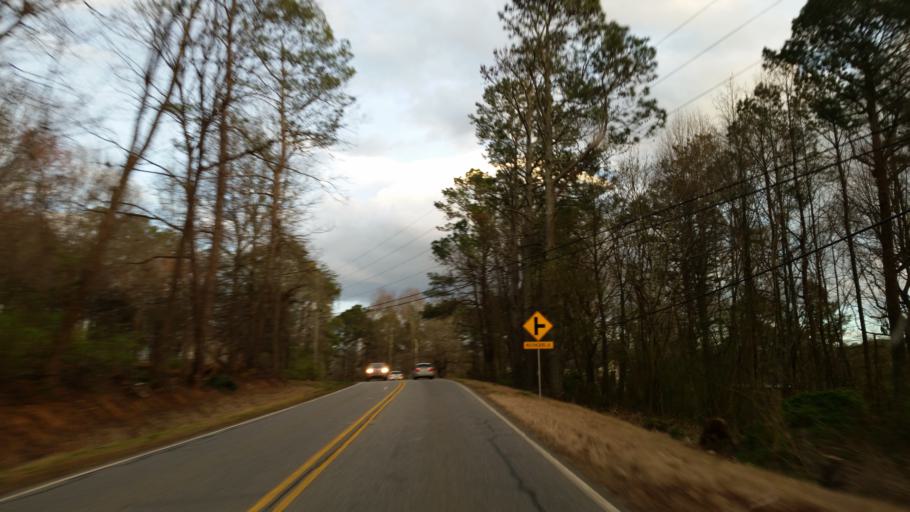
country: US
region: Georgia
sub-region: Pickens County
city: Jasper
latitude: 34.4651
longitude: -84.4783
